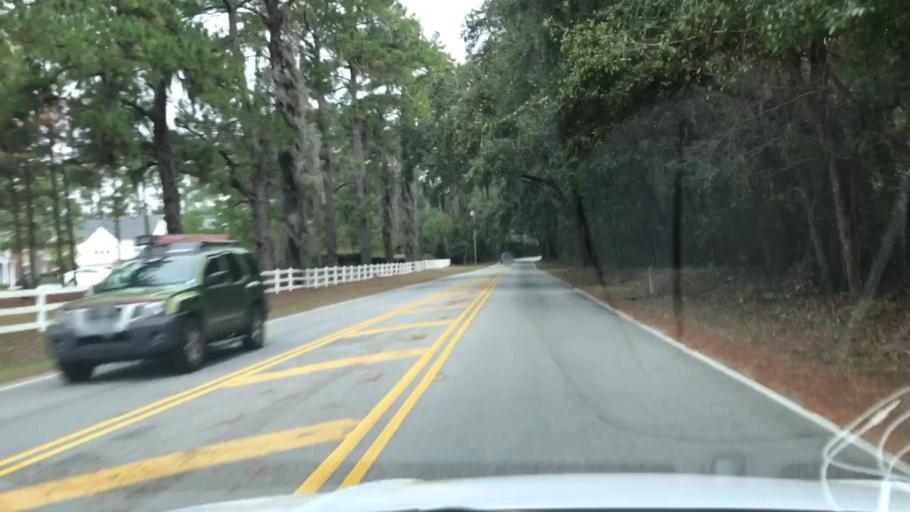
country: US
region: South Carolina
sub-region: Beaufort County
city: Bluffton
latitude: 32.2728
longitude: -80.8772
